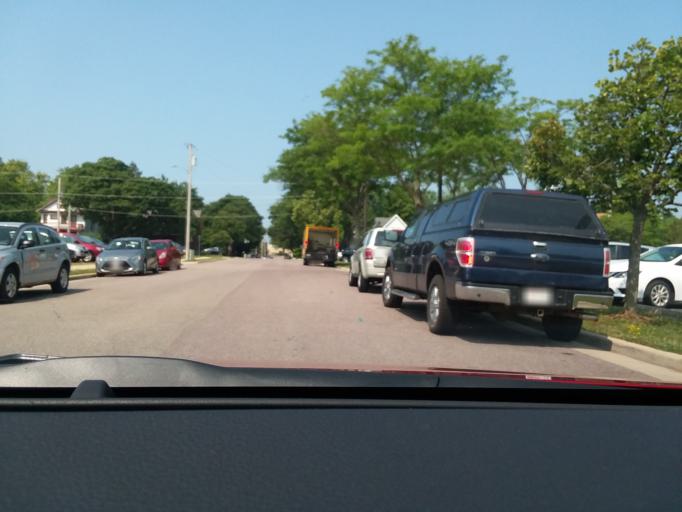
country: US
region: Wisconsin
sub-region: Dane County
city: Verona
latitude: 42.9883
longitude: -89.5337
